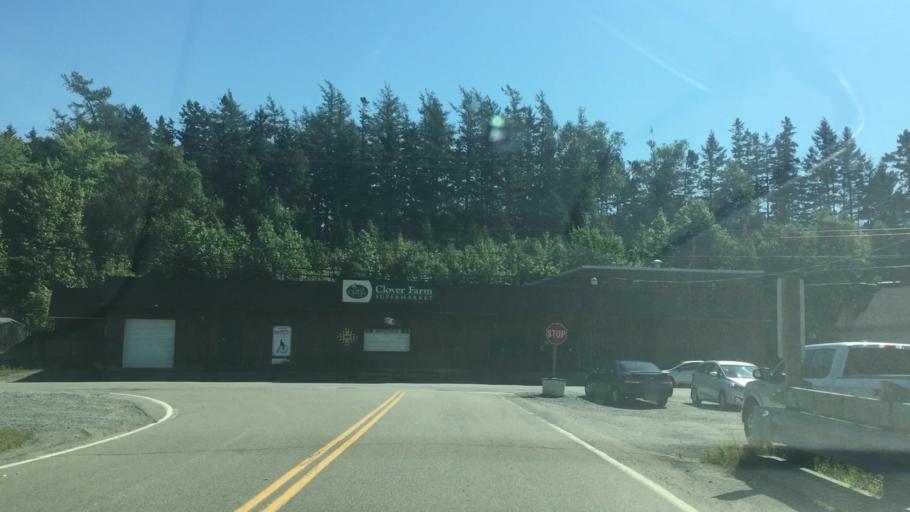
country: CA
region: Nova Scotia
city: Antigonish
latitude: 45.1427
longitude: -61.9831
